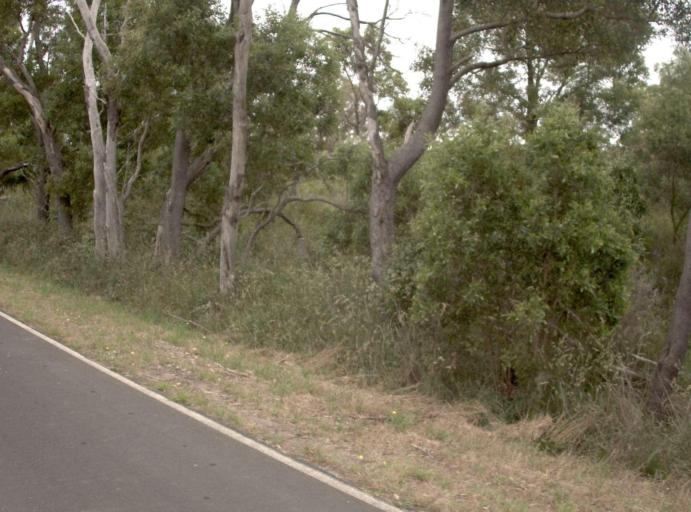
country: AU
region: Victoria
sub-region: Latrobe
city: Traralgon
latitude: -38.4866
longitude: 146.8200
